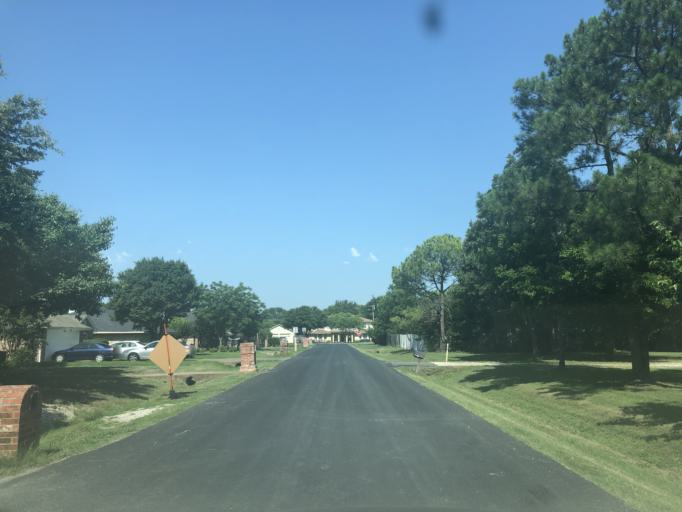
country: US
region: Texas
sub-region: Dallas County
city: Grand Prairie
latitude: 32.7156
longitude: -97.0004
